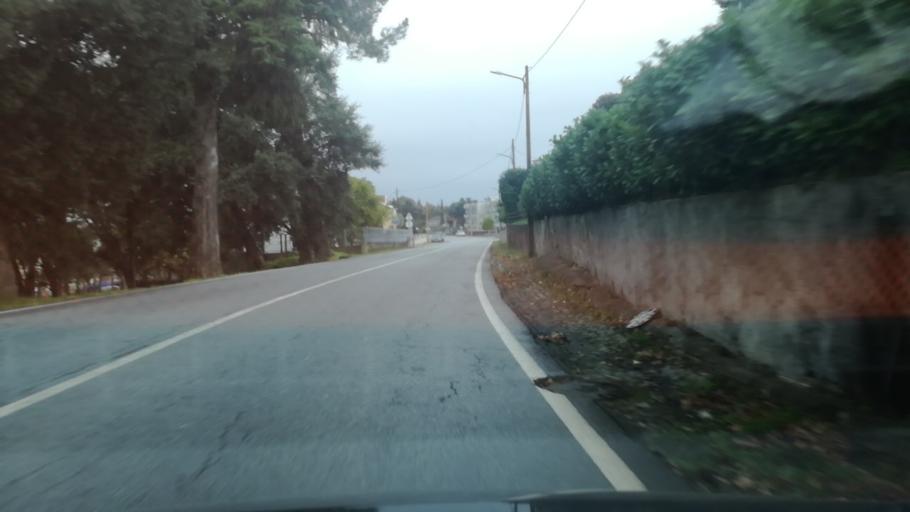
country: PT
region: Braga
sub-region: Braga
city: Braga
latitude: 41.5317
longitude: -8.4015
